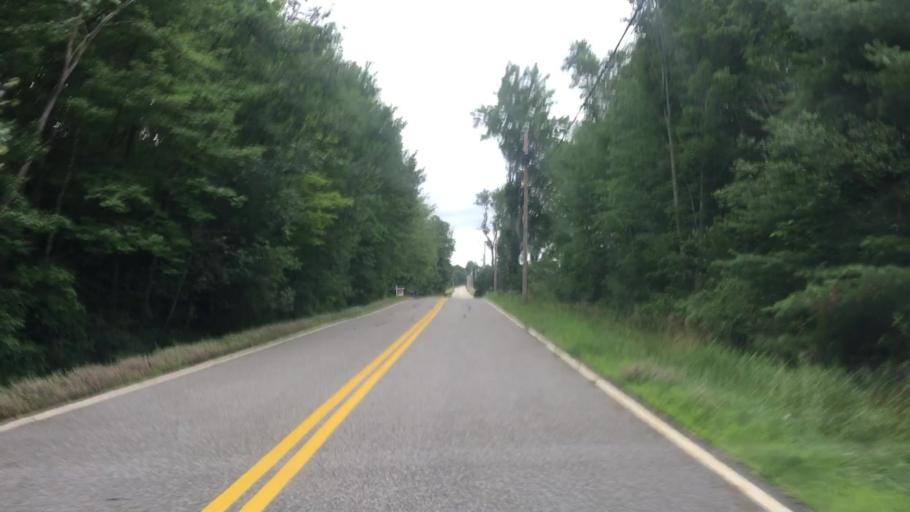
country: US
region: Maine
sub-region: York County
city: Biddeford
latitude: 43.5271
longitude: -70.5073
